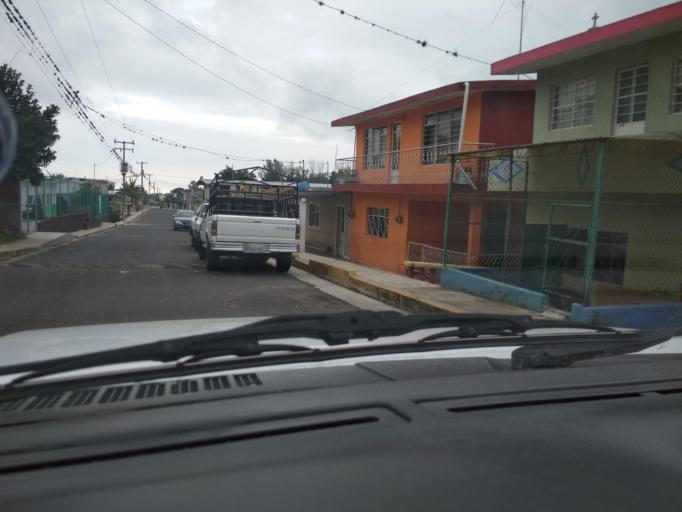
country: MX
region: Veracruz
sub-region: Emiliano Zapata
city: Dos Rios
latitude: 19.5242
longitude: -96.7987
